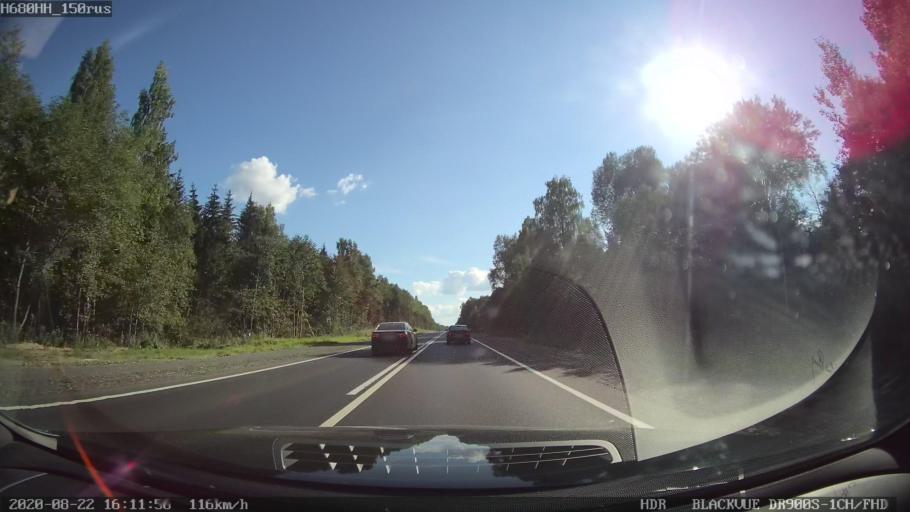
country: RU
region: Tverskaya
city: Rameshki
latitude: 57.4950
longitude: 36.2545
